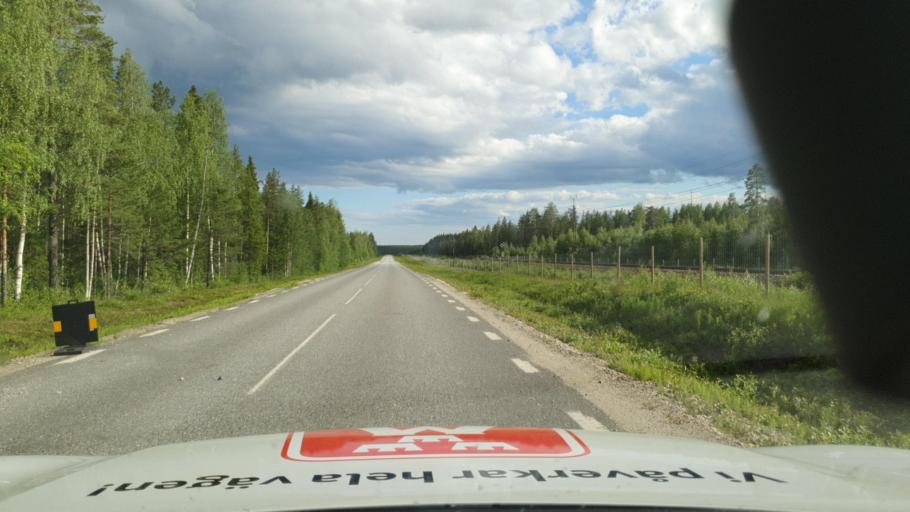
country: SE
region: Vaesterbotten
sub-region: Vindelns Kommun
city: Vindeln
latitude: 64.3779
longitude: 19.6587
